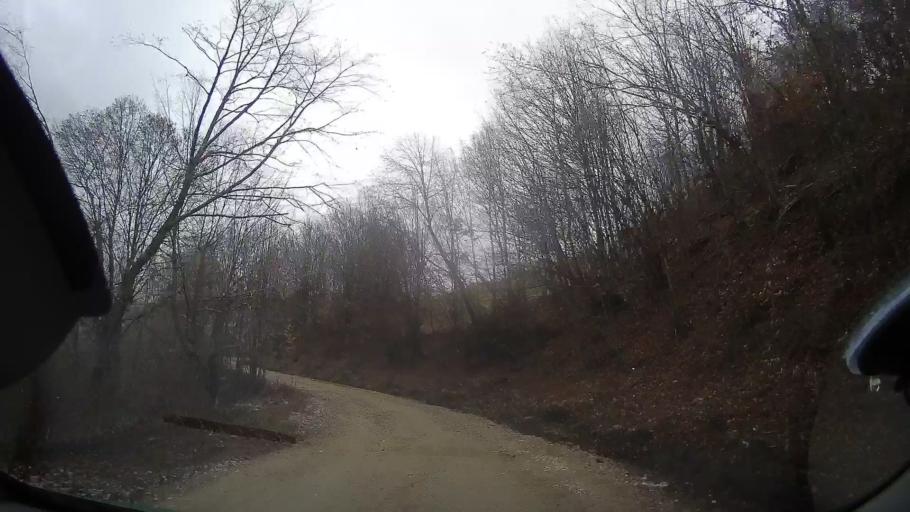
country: RO
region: Cluj
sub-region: Comuna Maguri-Racatau
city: Maguri-Racatau
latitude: 46.6540
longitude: 23.1891
